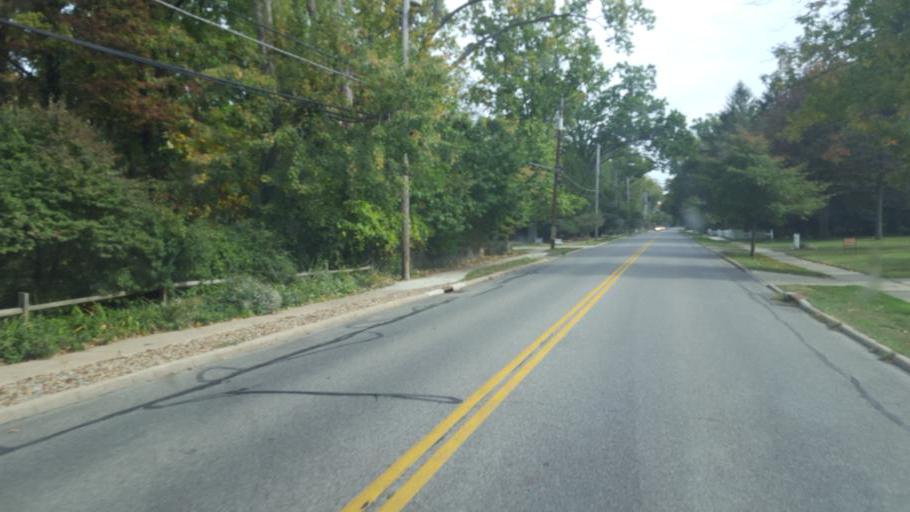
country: US
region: Ohio
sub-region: Cuyahoga County
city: Bay Village
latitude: 41.5004
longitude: -81.9628
